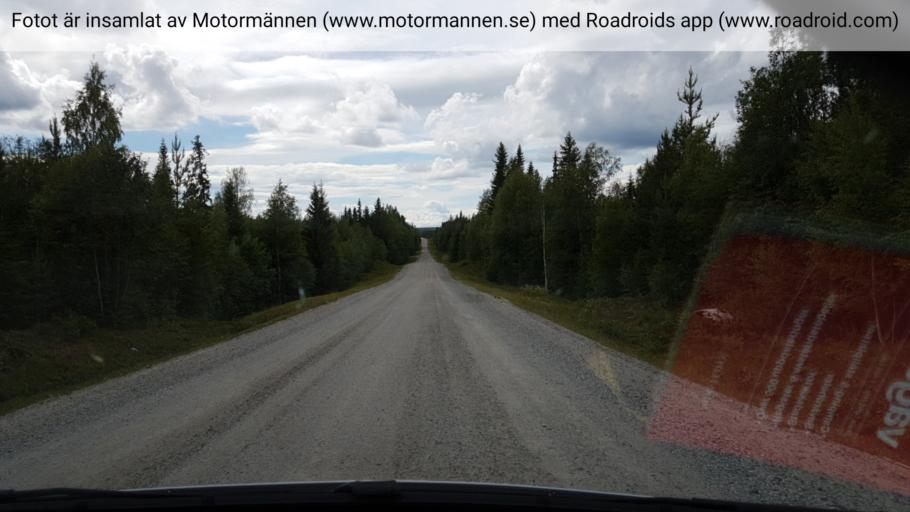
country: SE
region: Vaesternorrland
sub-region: Solleftea Kommun
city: Solleftea
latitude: 63.3373
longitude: 17.4399
